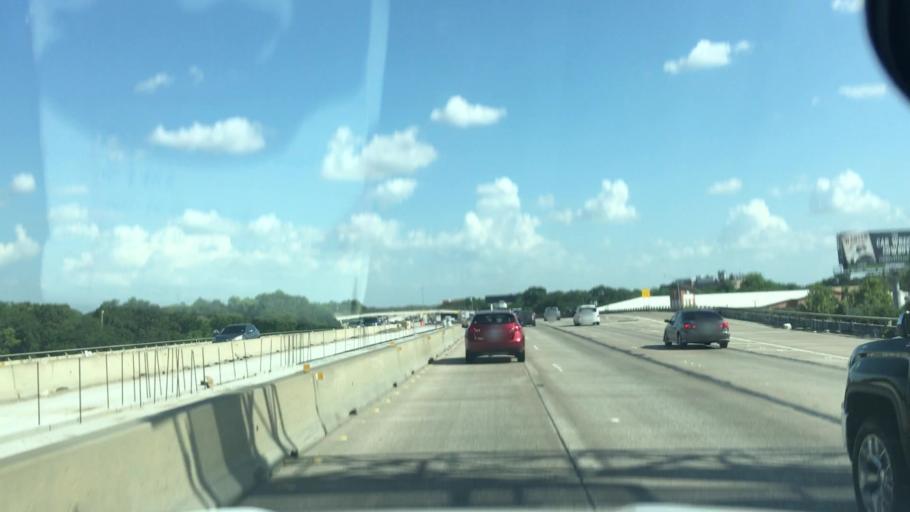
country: US
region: Texas
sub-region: Dallas County
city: Dallas
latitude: 32.7622
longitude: -96.7751
